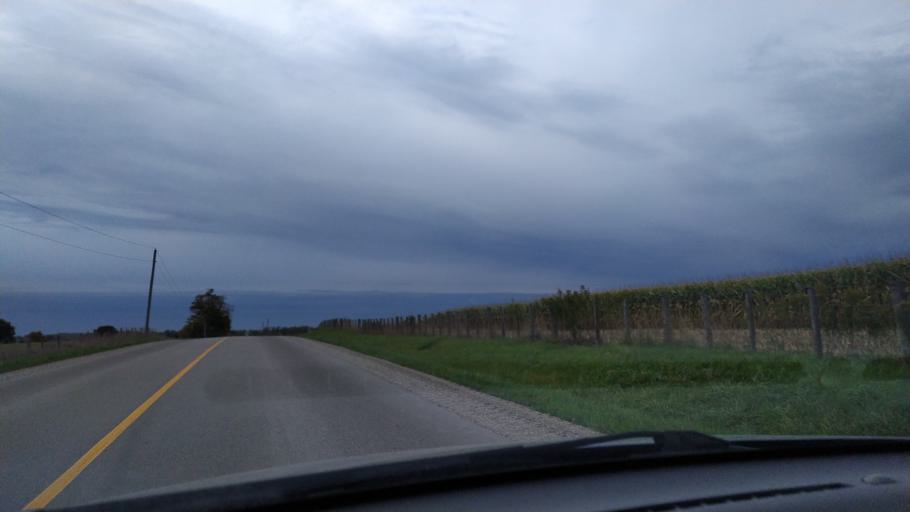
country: CA
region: Ontario
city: Waterloo
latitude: 43.5105
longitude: -80.7205
